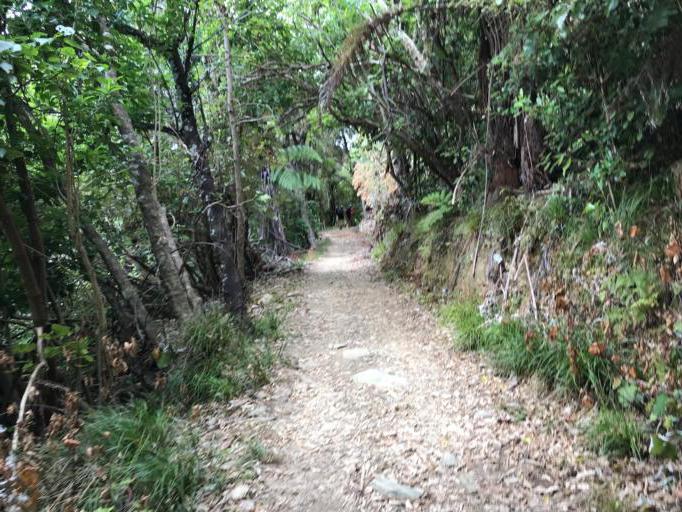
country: NZ
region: Marlborough
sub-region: Marlborough District
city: Picton
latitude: -41.1163
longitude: 174.2041
